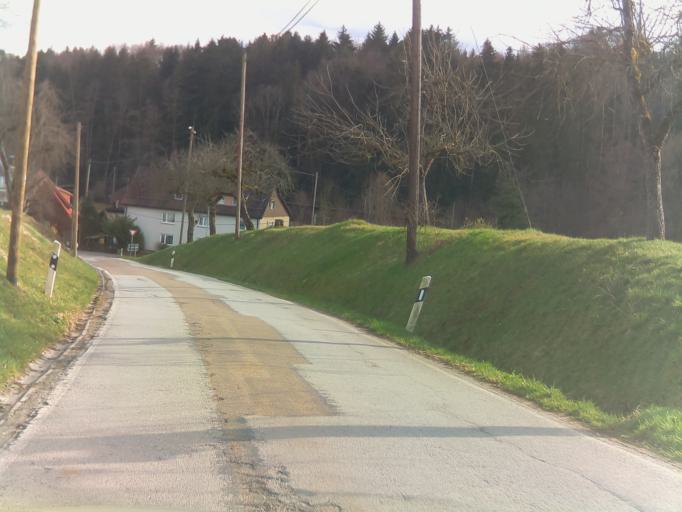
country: DE
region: Baden-Wuerttemberg
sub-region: Regierungsbezirk Stuttgart
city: Lorch
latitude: 48.8098
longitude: 9.6557
